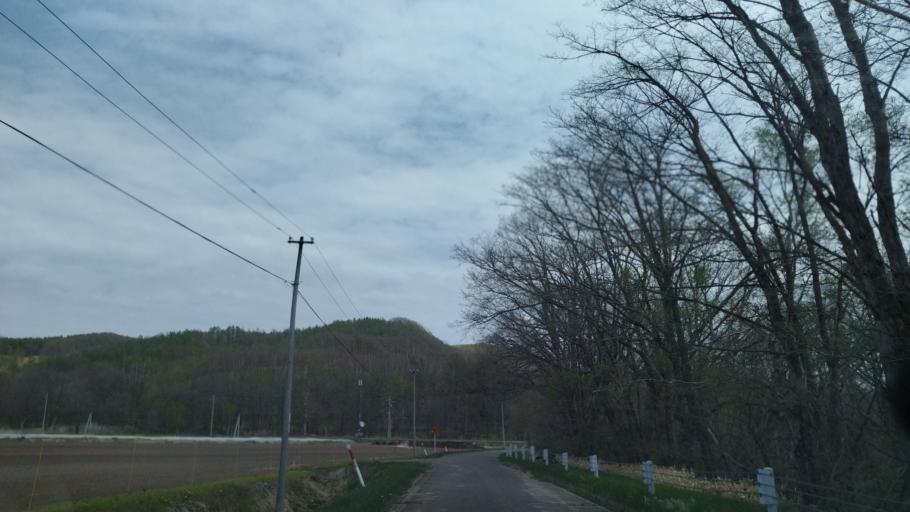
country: JP
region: Hokkaido
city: Otofuke
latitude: 43.3142
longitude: 143.5788
